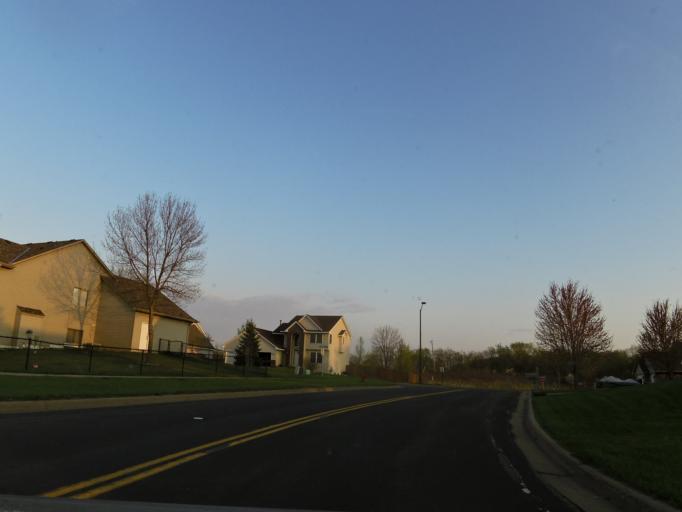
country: US
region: Minnesota
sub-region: Scott County
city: Prior Lake
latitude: 44.7406
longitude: -93.4288
